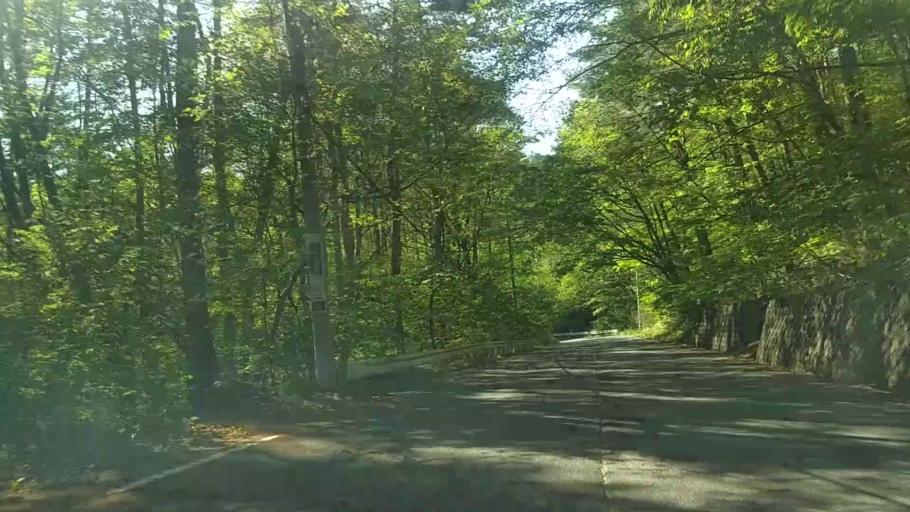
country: JP
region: Yamanashi
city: Nirasaki
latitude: 35.8920
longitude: 138.4002
